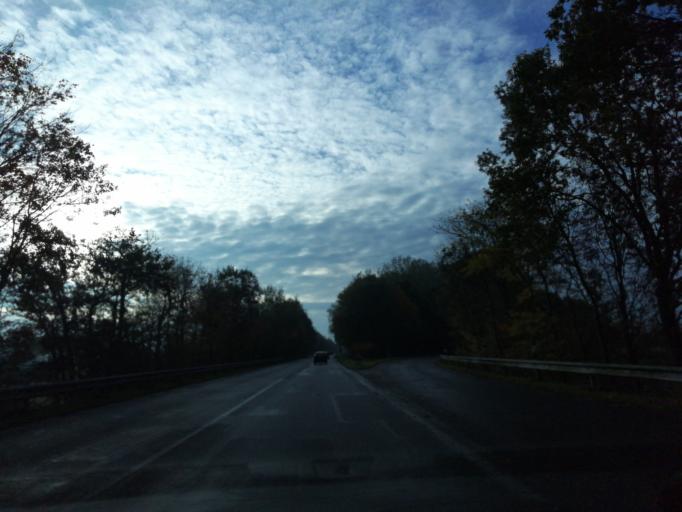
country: DE
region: Lower Saxony
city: Fedderwarden
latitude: 53.5967
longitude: 8.0521
